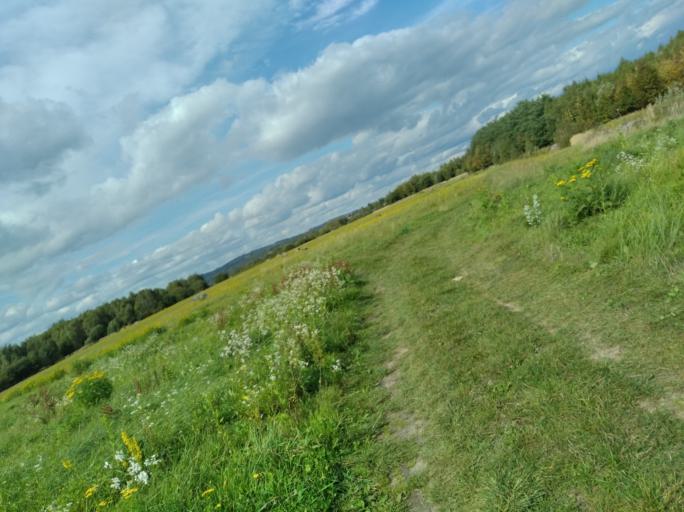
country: PL
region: Subcarpathian Voivodeship
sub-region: Powiat strzyzowski
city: Jawornik
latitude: 49.8340
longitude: 21.9084
